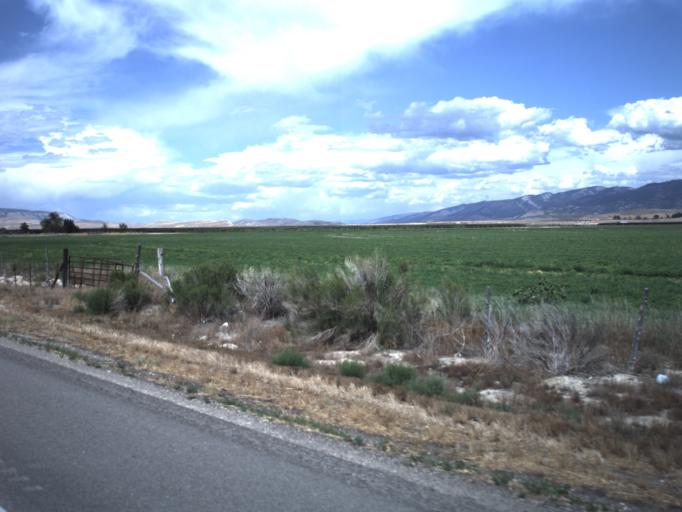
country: US
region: Utah
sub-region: Sanpete County
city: Centerfield
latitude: 39.0907
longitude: -111.8200
